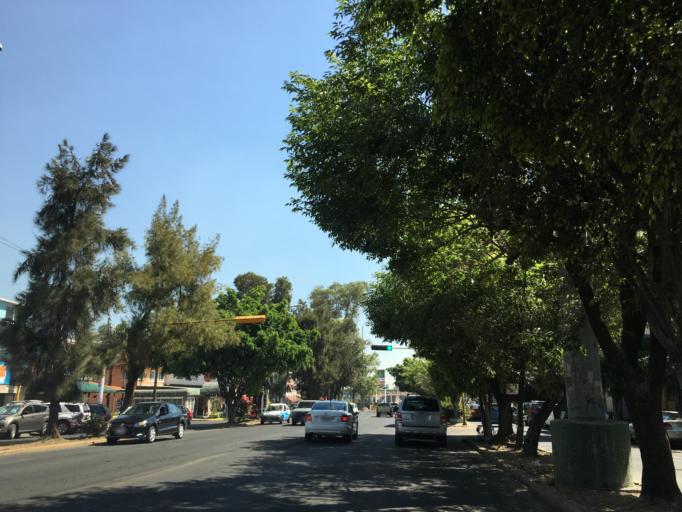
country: MX
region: Jalisco
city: Guadalajara
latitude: 20.6267
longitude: -103.4110
